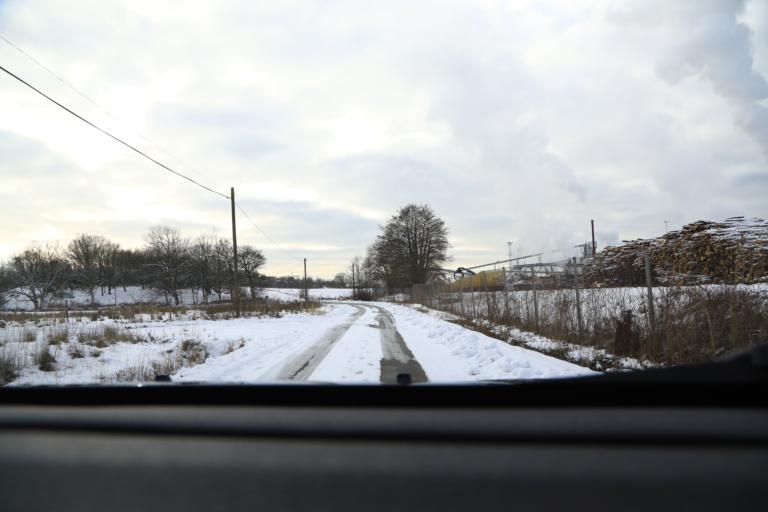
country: SE
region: Halland
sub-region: Kungsbacka Kommun
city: Frillesas
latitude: 57.2235
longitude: 12.1864
